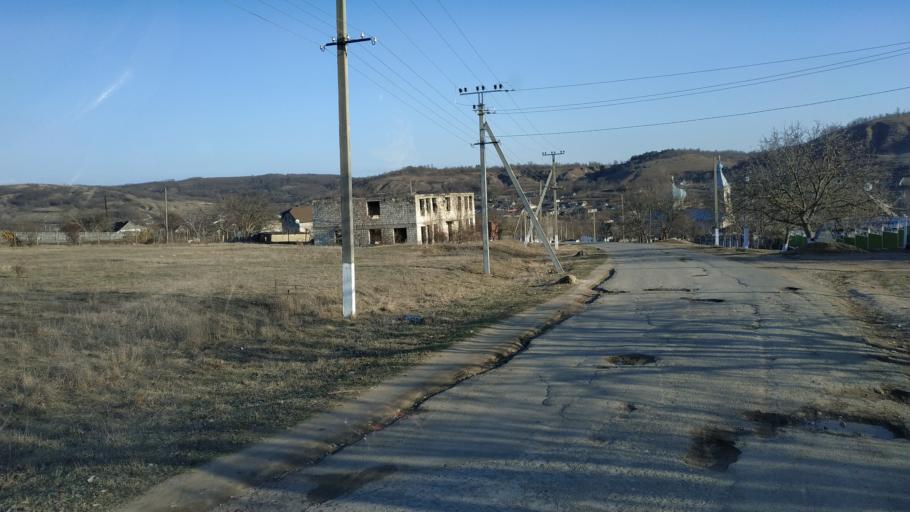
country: MD
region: Hincesti
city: Hincesti
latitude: 46.7011
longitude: 28.5422
